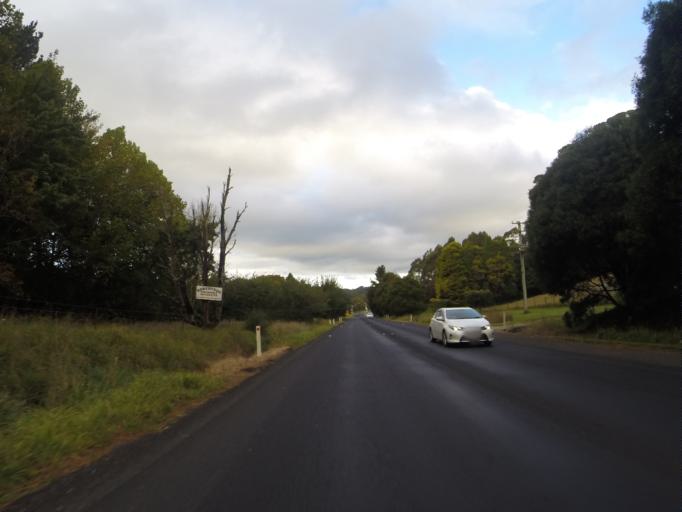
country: AU
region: New South Wales
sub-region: Shellharbour
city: Calderwood
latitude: -34.5877
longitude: 150.5817
